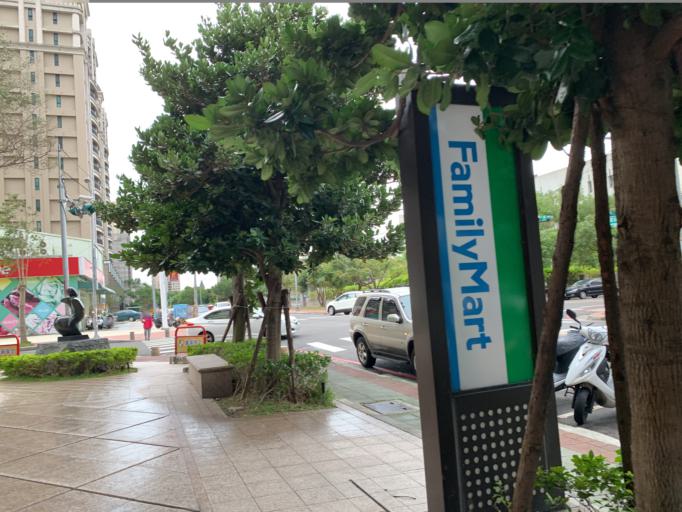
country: TW
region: Taiwan
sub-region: Hsinchu
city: Zhubei
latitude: 24.8176
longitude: 121.0182
